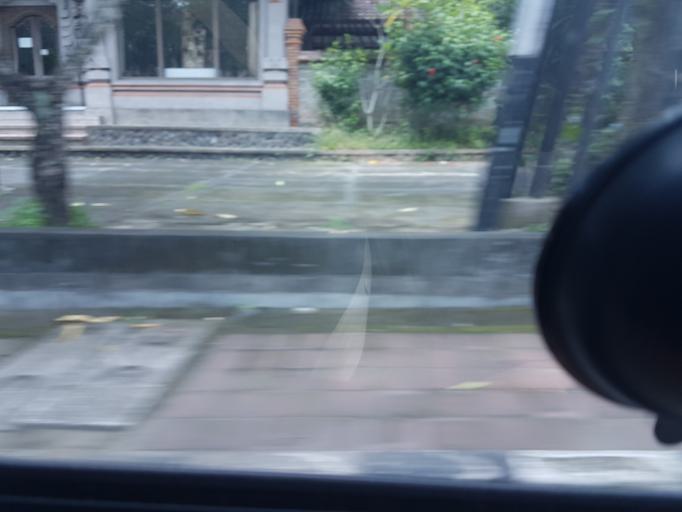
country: ID
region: Bali
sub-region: Kabupaten Gianyar
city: Ubud
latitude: -8.5329
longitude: 115.2722
